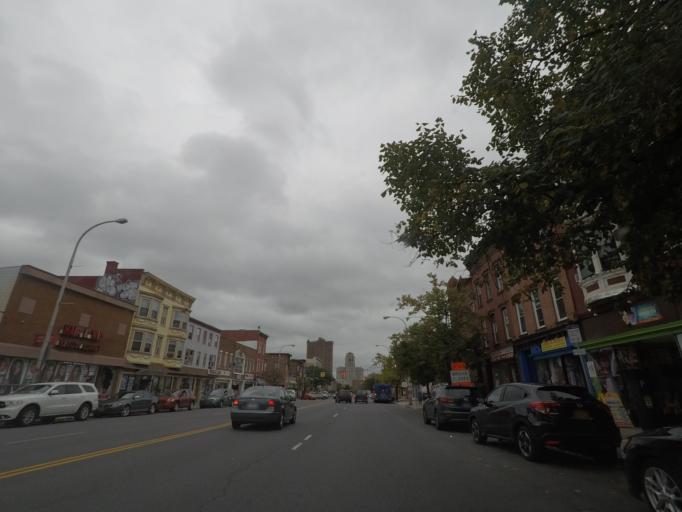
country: US
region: New York
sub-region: Albany County
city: Albany
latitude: 42.6608
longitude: -73.7680
